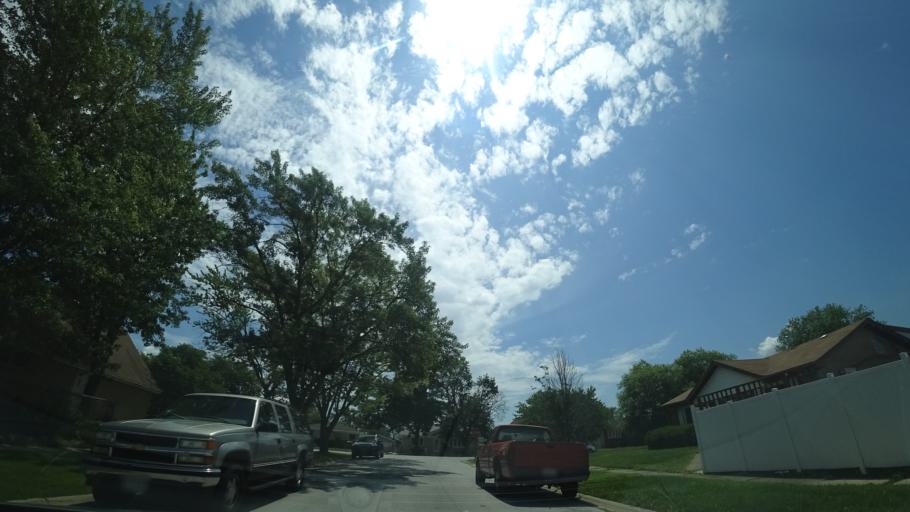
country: US
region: Illinois
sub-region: Cook County
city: Alsip
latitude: 41.6678
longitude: -87.7316
